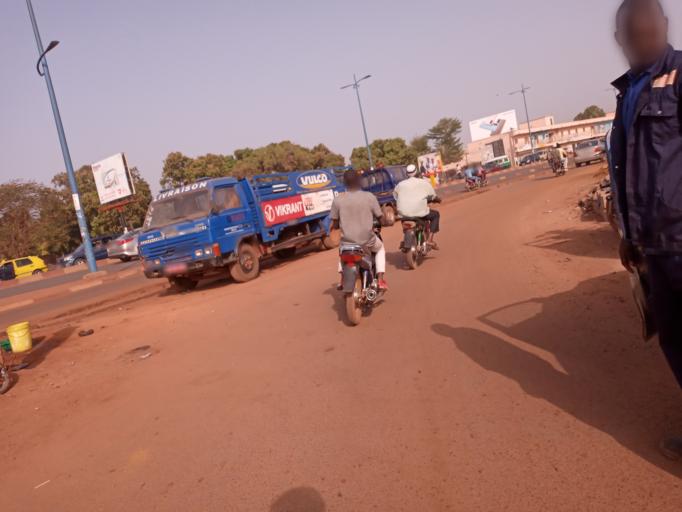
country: ML
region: Bamako
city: Bamako
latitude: 12.6098
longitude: -7.9755
